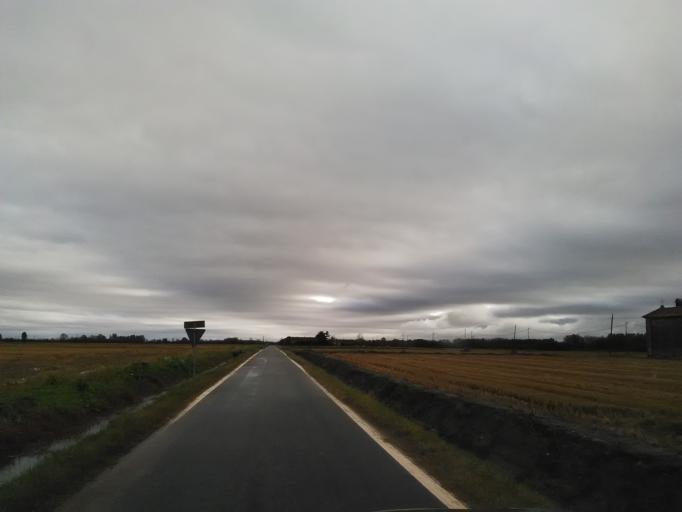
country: IT
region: Piedmont
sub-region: Provincia di Vercelli
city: Casanova Elvo
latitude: 45.4083
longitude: 8.2487
